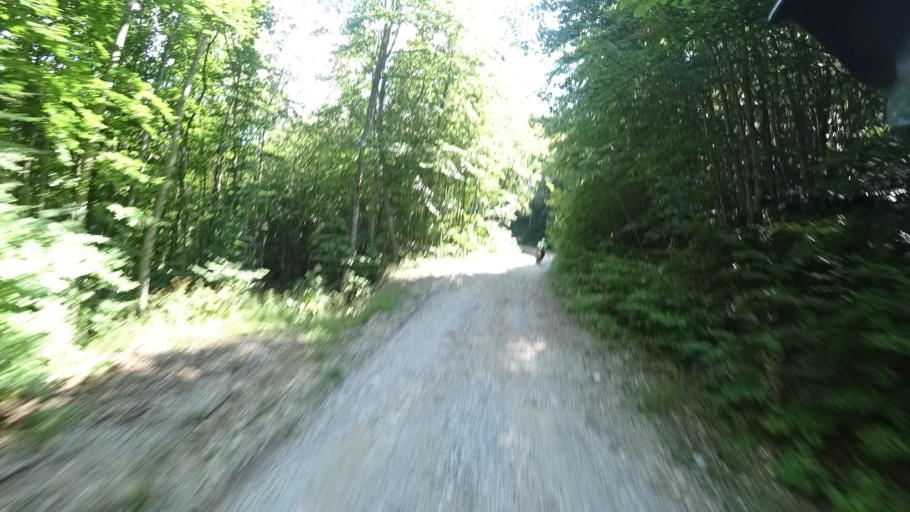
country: HR
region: Zadarska
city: Gracac
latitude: 44.4508
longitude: 15.9823
